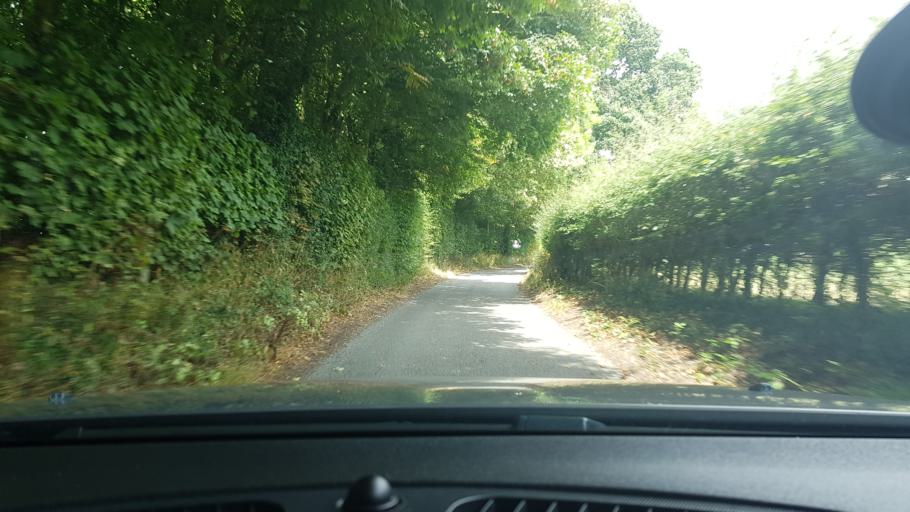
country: GB
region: England
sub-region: West Berkshire
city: Hungerford
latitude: 51.4327
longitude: -1.5192
